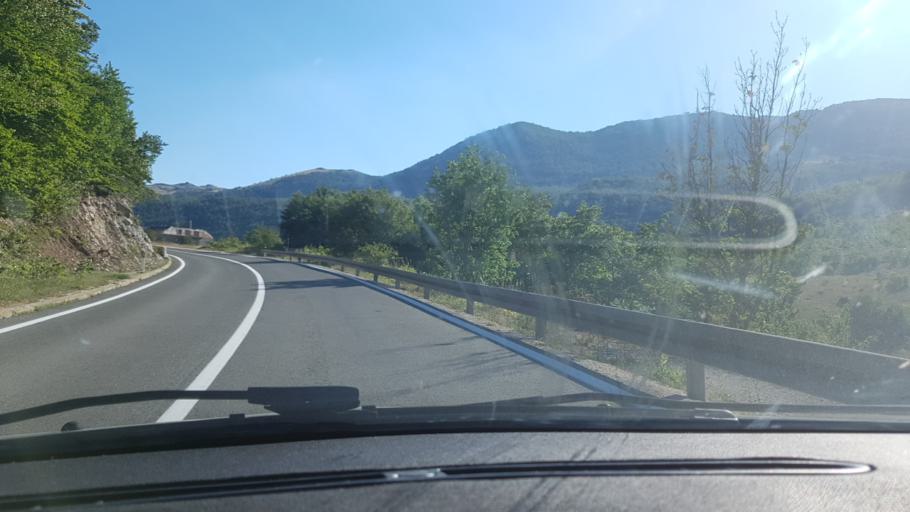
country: HR
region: Zadarska
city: Gracac
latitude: 44.2692
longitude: 15.8117
